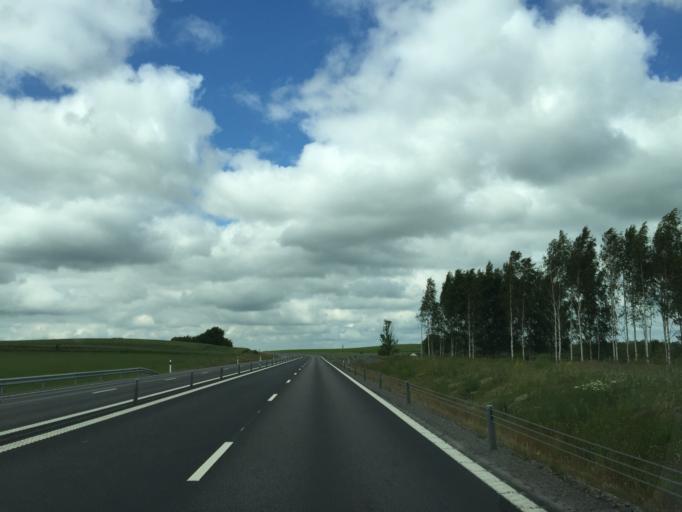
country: SE
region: Skane
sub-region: Svedala Kommun
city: Klagerup
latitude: 55.5666
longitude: 13.2557
